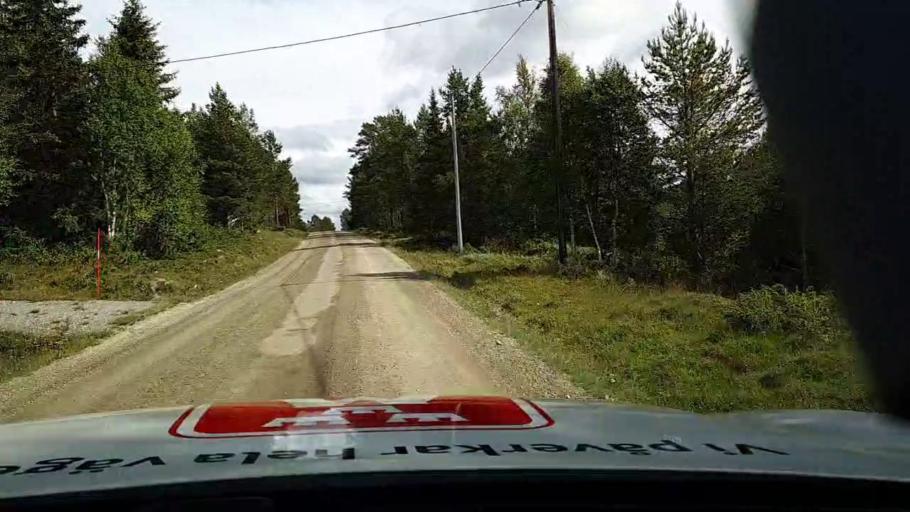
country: SE
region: Jaemtland
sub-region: Are Kommun
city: Jarpen
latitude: 62.5508
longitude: 13.4478
